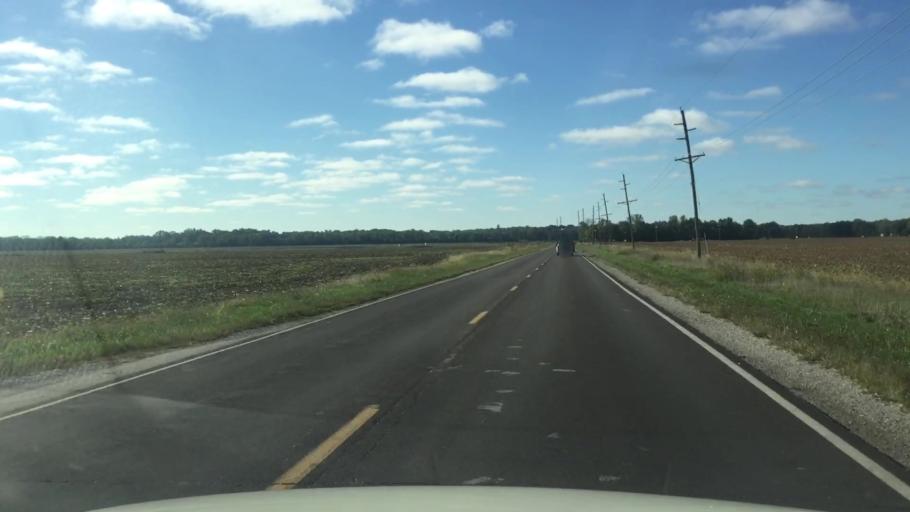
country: US
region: Missouri
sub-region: Howard County
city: New Franklin
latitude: 39.0051
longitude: -92.7383
